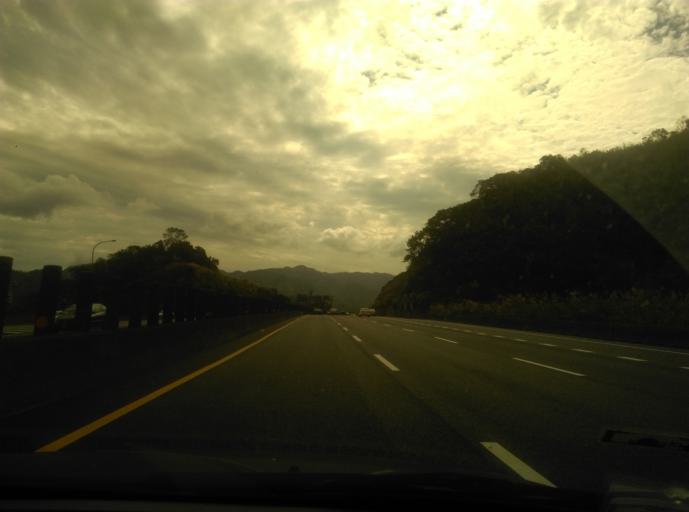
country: TW
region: Taiwan
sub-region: Keelung
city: Keelung
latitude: 25.0922
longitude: 121.6962
